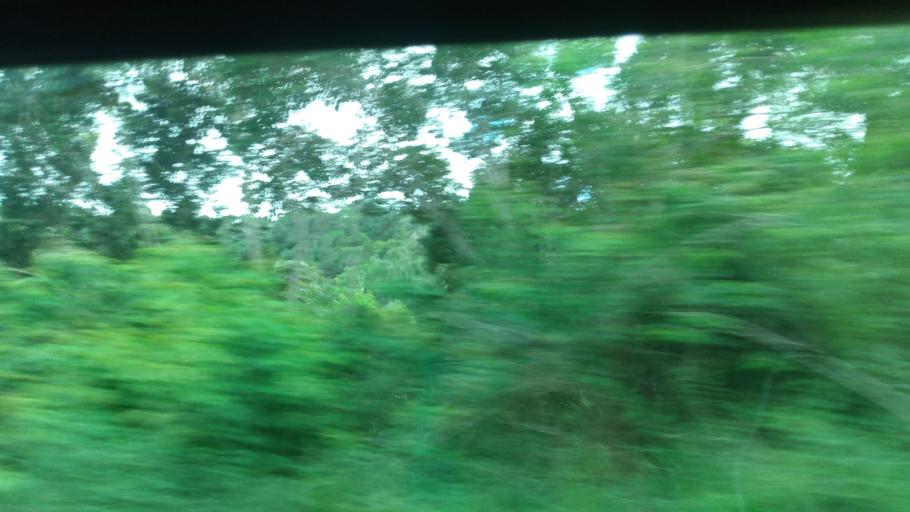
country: BR
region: Pernambuco
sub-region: Maraial
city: Maraial
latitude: -8.7831
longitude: -35.9092
